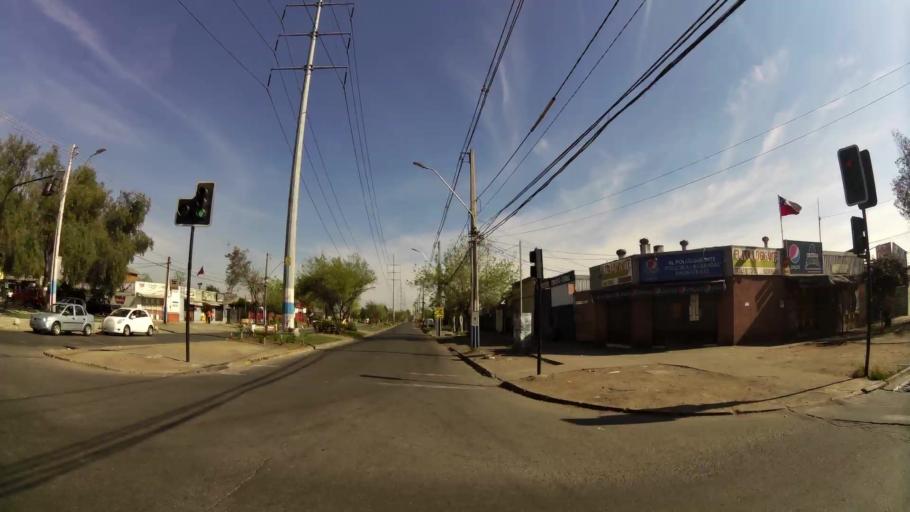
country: CL
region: Santiago Metropolitan
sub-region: Provincia de Santiago
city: Villa Presidente Frei, Nunoa, Santiago, Chile
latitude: -33.4642
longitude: -70.5663
